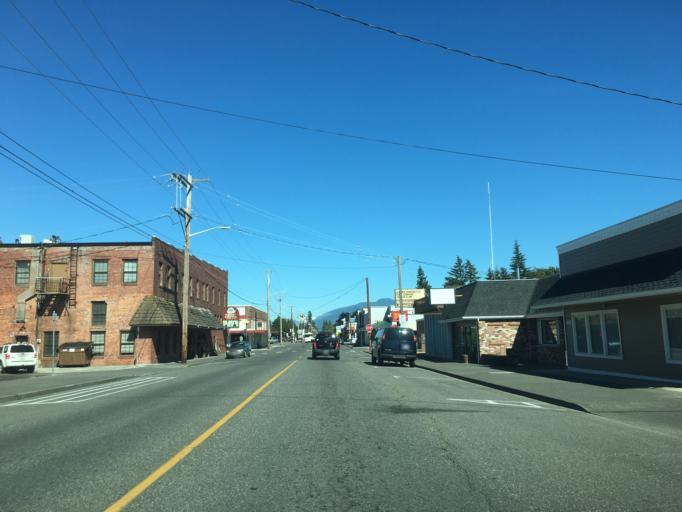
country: US
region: Washington
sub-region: Skagit County
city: Sedro-Woolley
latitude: 48.5033
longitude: -122.2398
